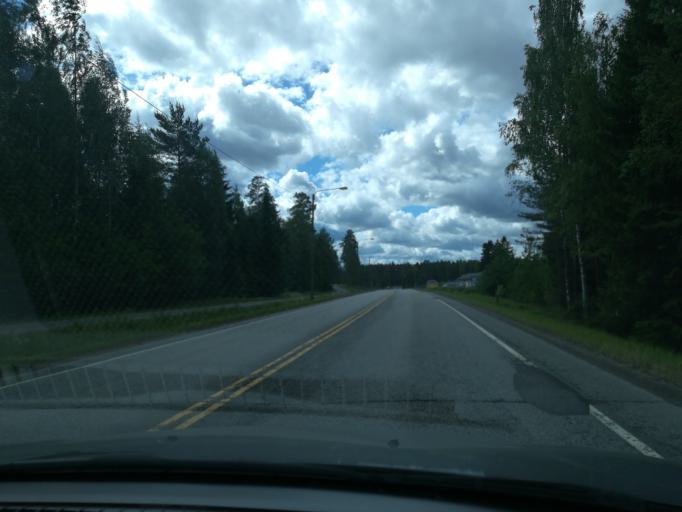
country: FI
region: Southern Savonia
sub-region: Mikkeli
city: Ristiina
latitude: 61.5031
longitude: 27.2376
